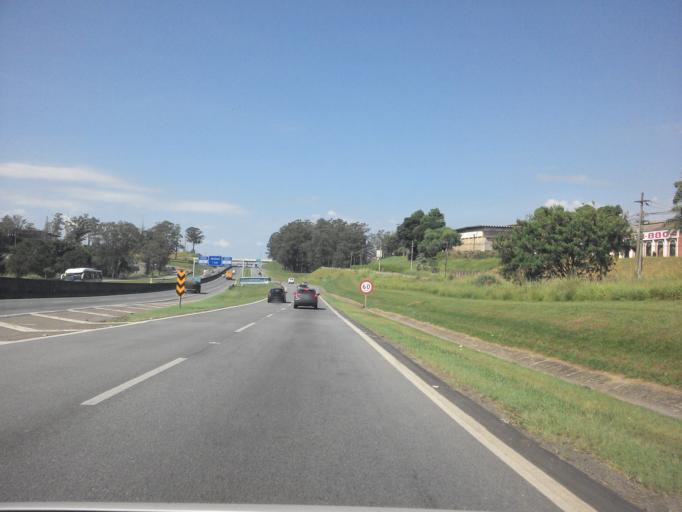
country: BR
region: Sao Paulo
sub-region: Valinhos
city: Valinhos
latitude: -23.0058
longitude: -47.0278
